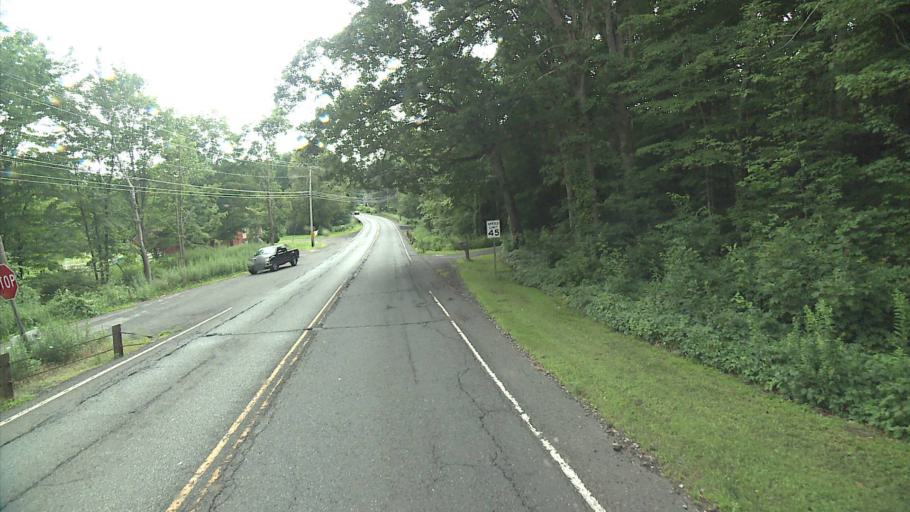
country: US
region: Connecticut
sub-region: New Haven County
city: Oxford
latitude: 41.4585
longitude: -73.1524
